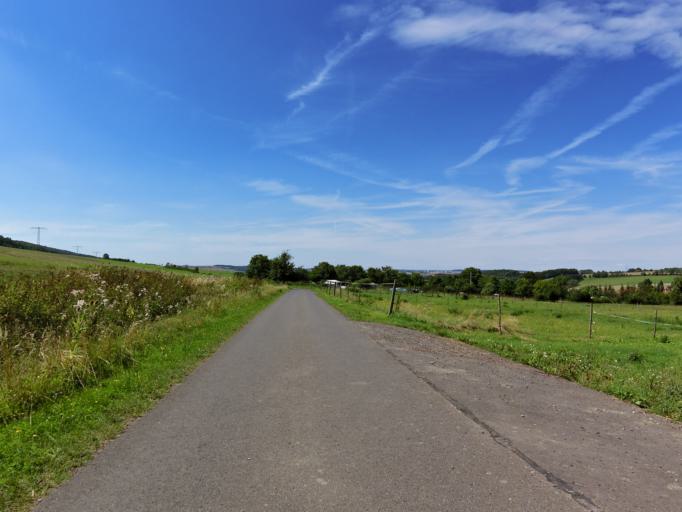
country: DE
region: Thuringia
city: Seebach
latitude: 50.9700
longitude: 10.4523
